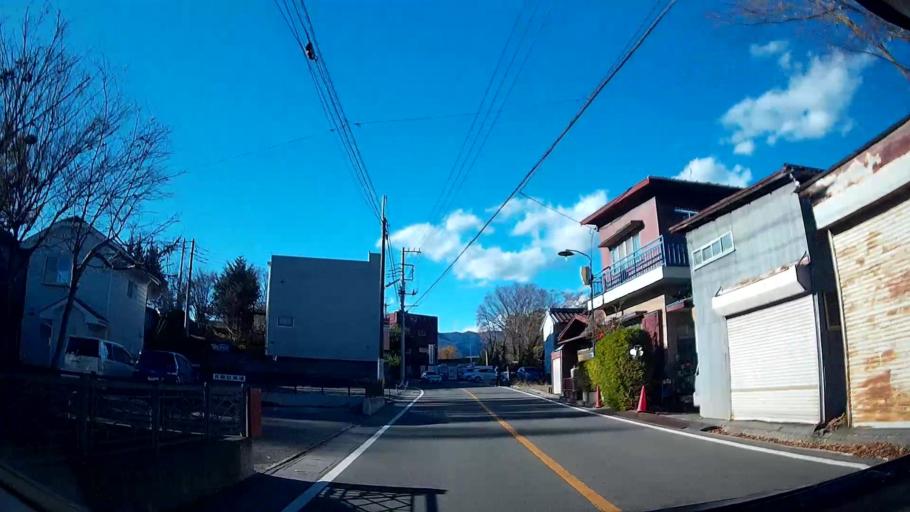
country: JP
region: Yamanashi
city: Fujikawaguchiko
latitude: 35.5015
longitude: 138.7630
